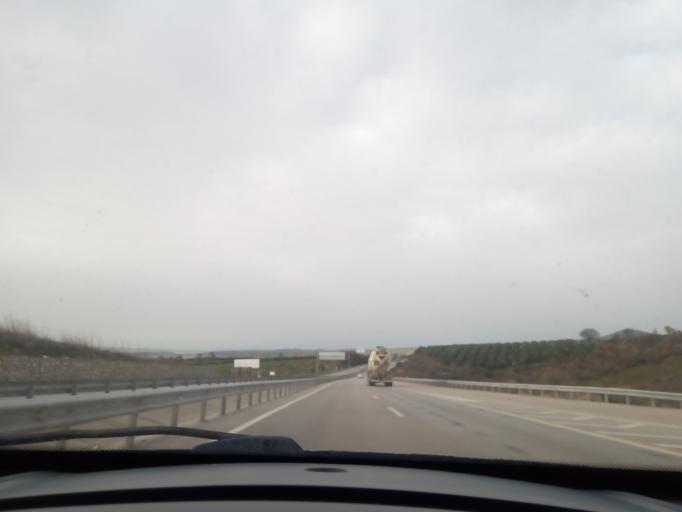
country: TR
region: Bursa
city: Gorukle
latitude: 40.2153
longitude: 28.7481
